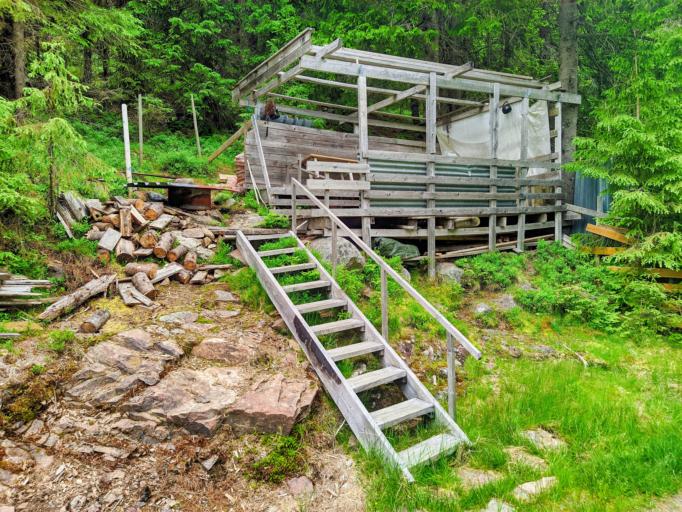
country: NO
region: Akershus
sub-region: Hurdal
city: Hurdal
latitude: 60.5589
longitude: 11.1276
